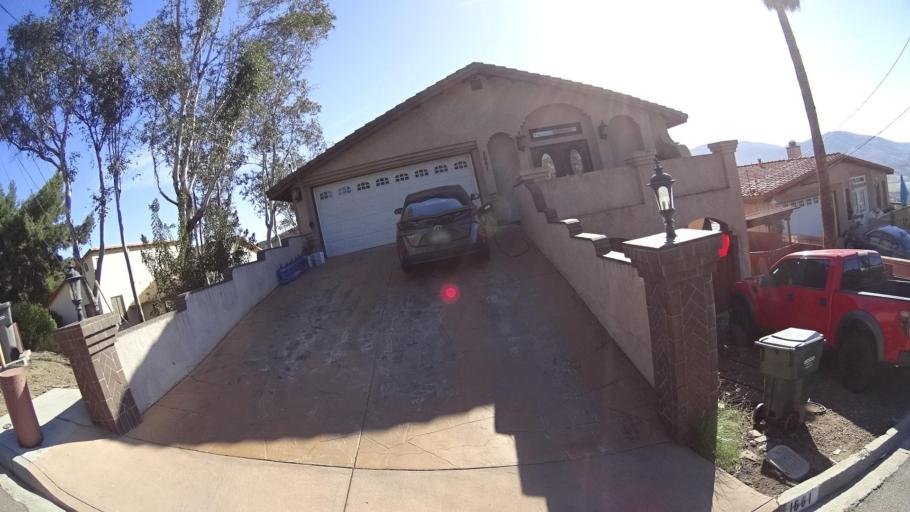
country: US
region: California
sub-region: San Diego County
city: La Presa
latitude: 32.7219
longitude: -116.9922
